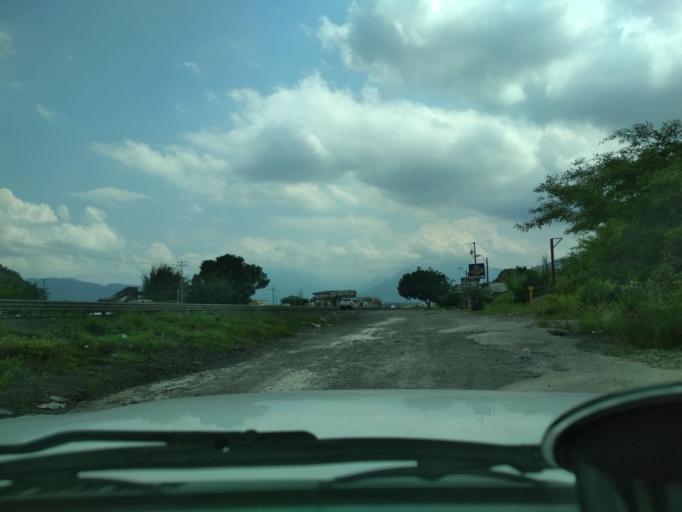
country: MX
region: Veracruz
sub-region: Ixtaczoquitlan
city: Buenavista
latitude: 18.8968
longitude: -97.0398
